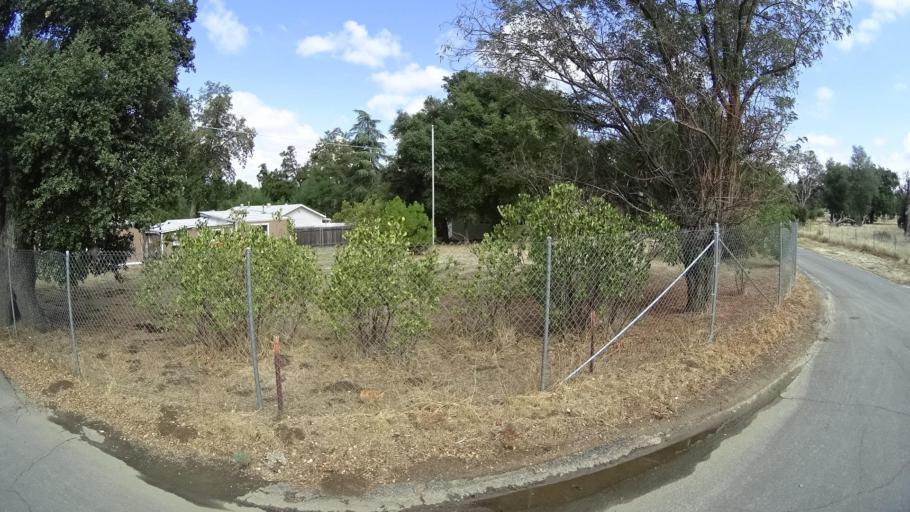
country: US
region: California
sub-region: San Diego County
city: Campo
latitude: 32.6787
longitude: -116.5129
